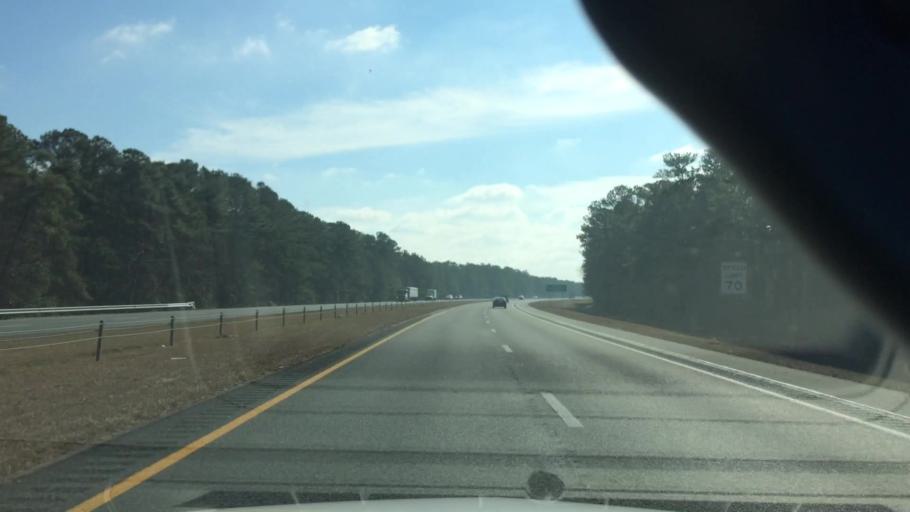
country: US
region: North Carolina
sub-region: Duplin County
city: Wallace
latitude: 34.7464
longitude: -77.9447
